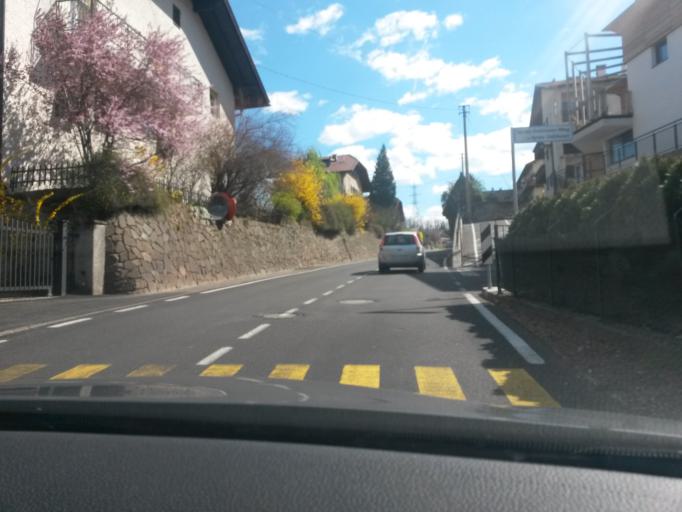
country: IT
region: Trentino-Alto Adige
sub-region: Bolzano
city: San Michele
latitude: 46.4515
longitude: 11.2714
